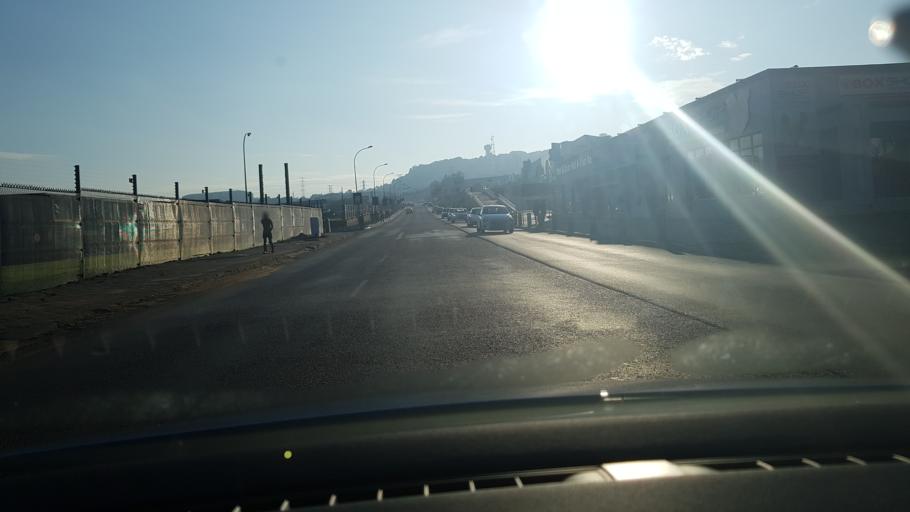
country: ZA
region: Gauteng
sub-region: Ekurhuleni Metropolitan Municipality
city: Germiston
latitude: -26.1680
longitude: 28.1619
